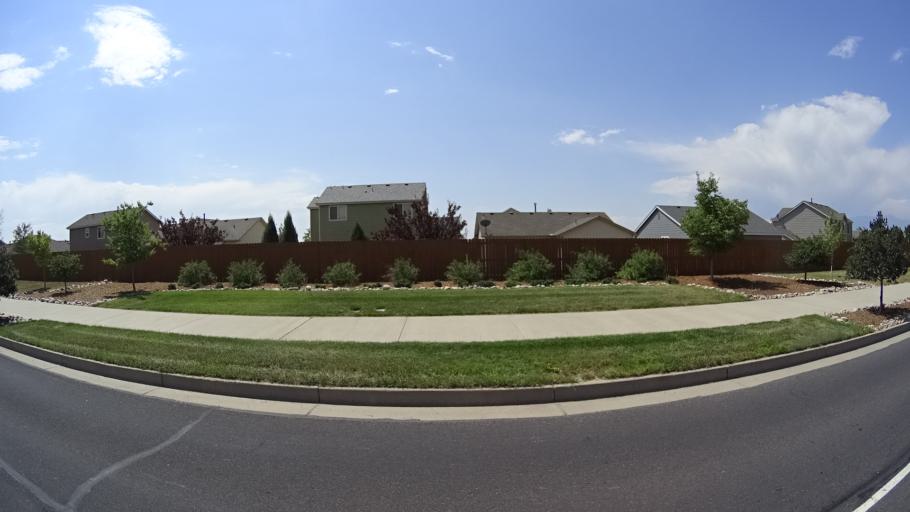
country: US
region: Colorado
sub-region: El Paso County
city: Cimarron Hills
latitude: 38.9259
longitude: -104.7096
